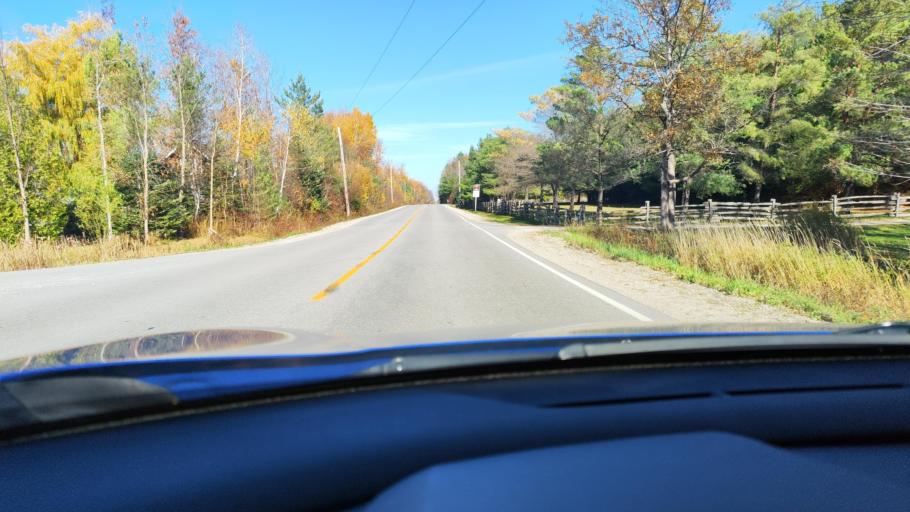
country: CA
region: Ontario
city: Wasaga Beach
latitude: 44.4050
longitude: -80.0589
